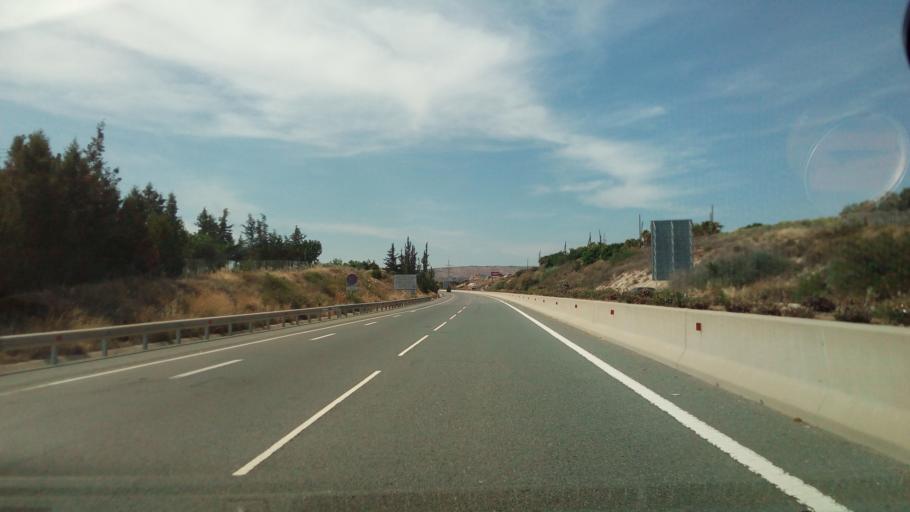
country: CY
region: Pafos
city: Mesogi
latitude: 34.7283
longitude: 32.5284
